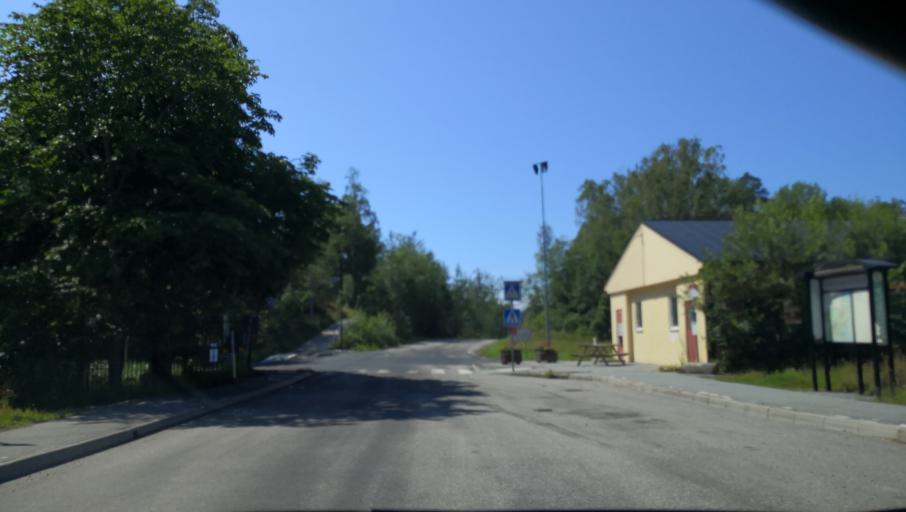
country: SE
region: Stockholm
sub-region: Varmdo Kommun
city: Mortnas
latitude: 59.3955
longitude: 18.4352
